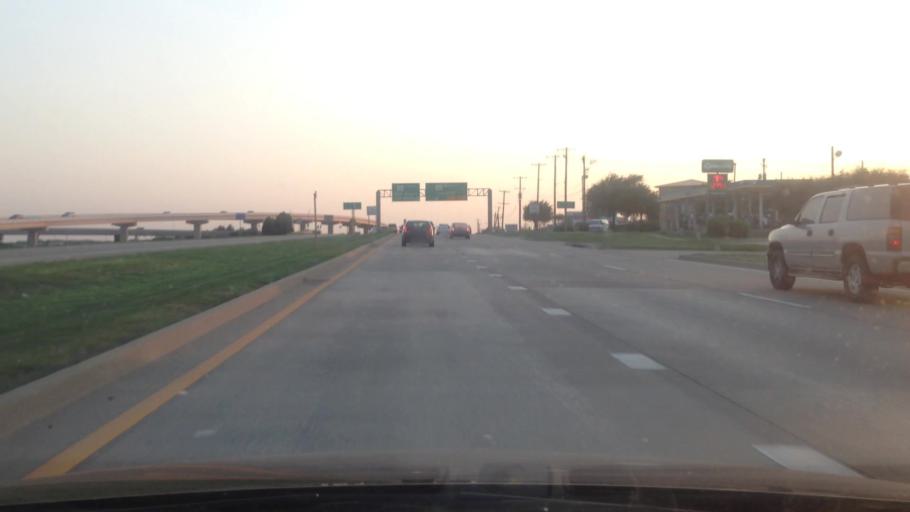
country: US
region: Texas
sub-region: Denton County
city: The Colony
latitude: 33.0535
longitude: -96.9168
